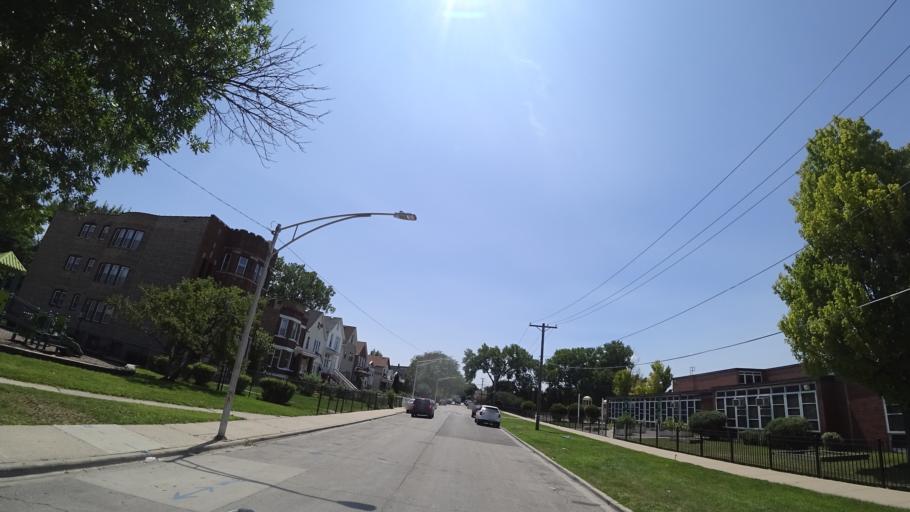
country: US
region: Illinois
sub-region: Cook County
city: Chicago
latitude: 41.7677
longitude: -87.5895
